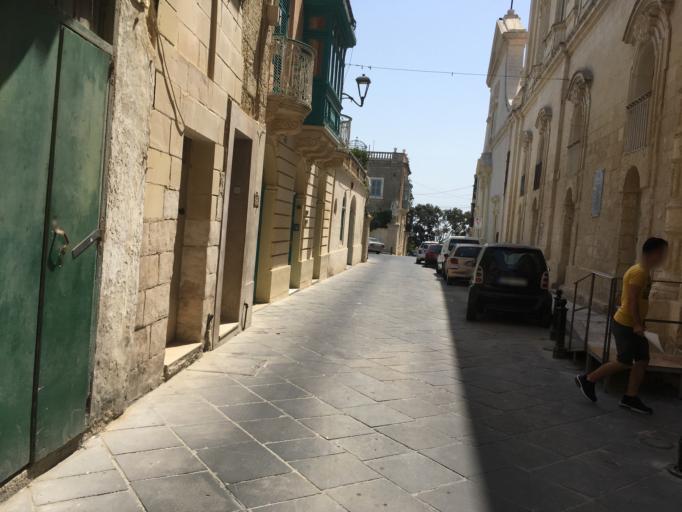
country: MT
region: Ir-Rabat
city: Rabat
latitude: 35.8830
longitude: 14.4018
